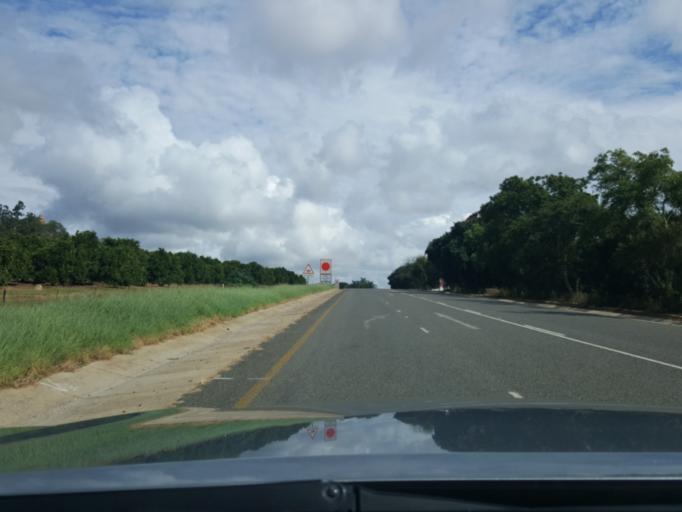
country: ZA
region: Mpumalanga
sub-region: Ehlanzeni District
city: Nelspruit
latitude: -25.4688
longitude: 31.0482
